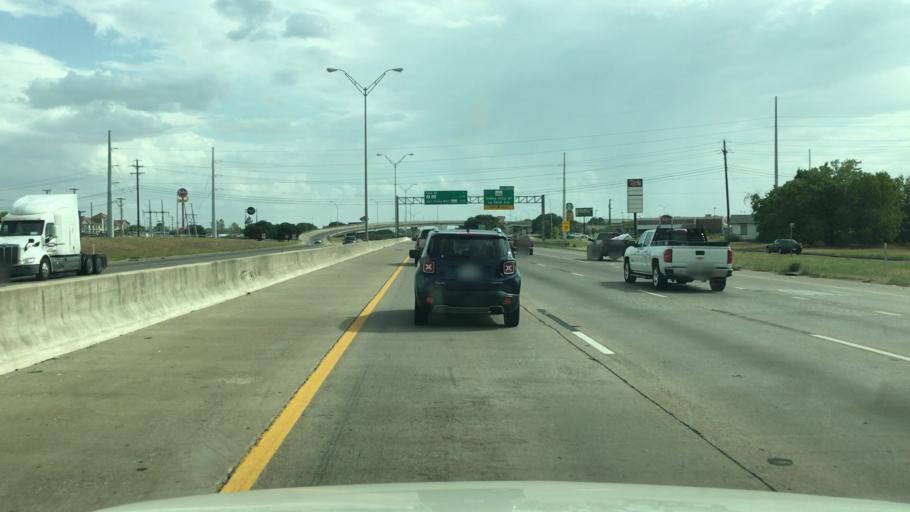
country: US
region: Texas
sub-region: McLennan County
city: Beverly
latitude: 31.5288
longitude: -97.1321
